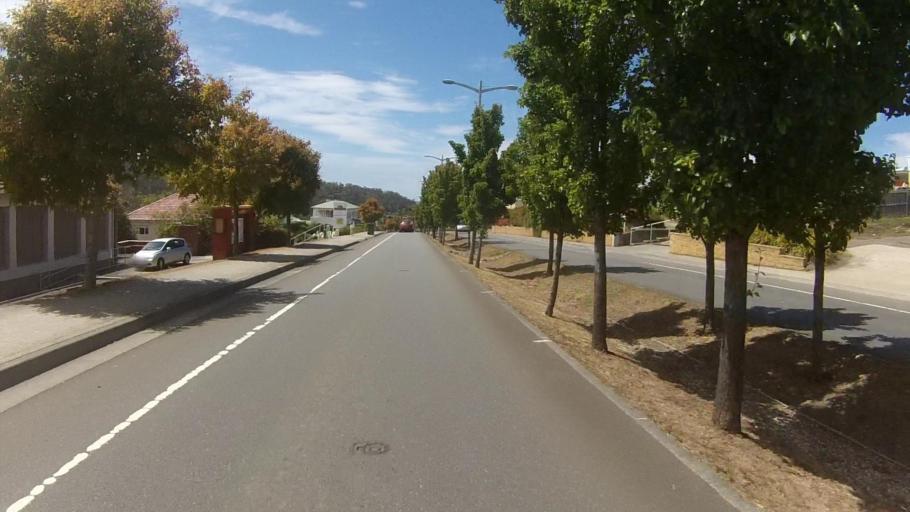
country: AU
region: Tasmania
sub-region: Kingborough
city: Kingston
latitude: -42.9757
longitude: 147.3060
